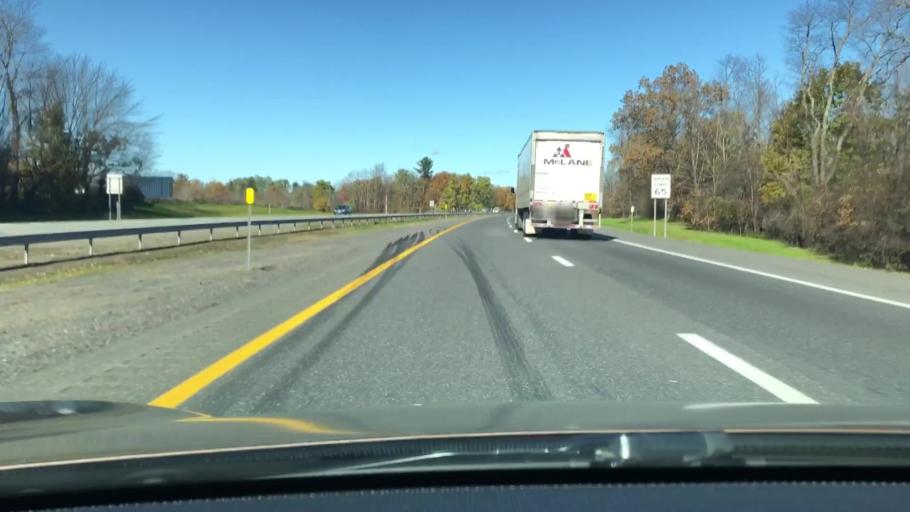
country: US
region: New York
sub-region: Ulster County
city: Plattekill
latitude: 41.5842
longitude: -74.0886
